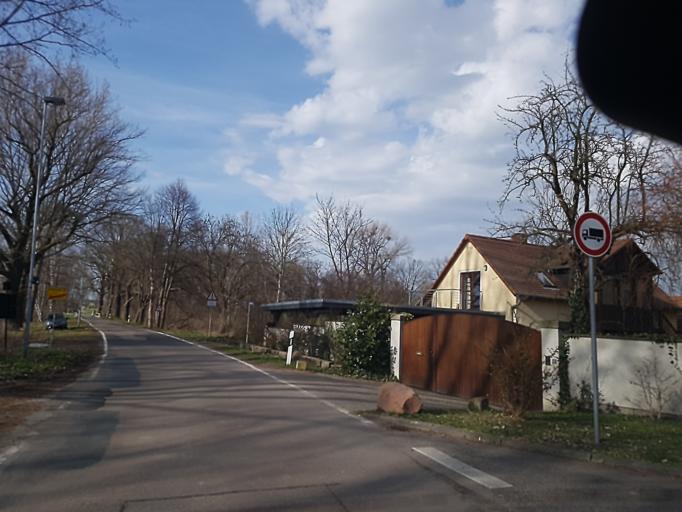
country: DE
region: Saxony
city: Strehla
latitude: 51.3062
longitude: 13.1813
